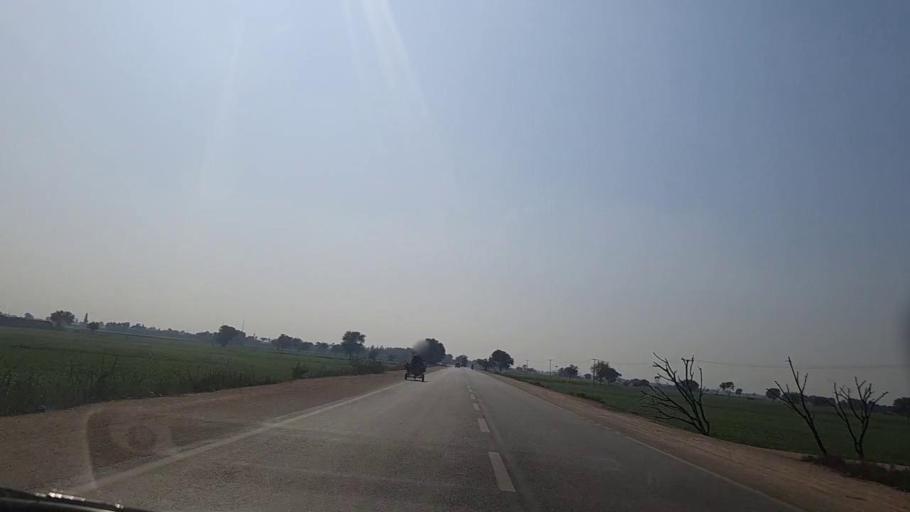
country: PK
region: Sindh
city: Hala
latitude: 25.9921
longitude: 68.3895
